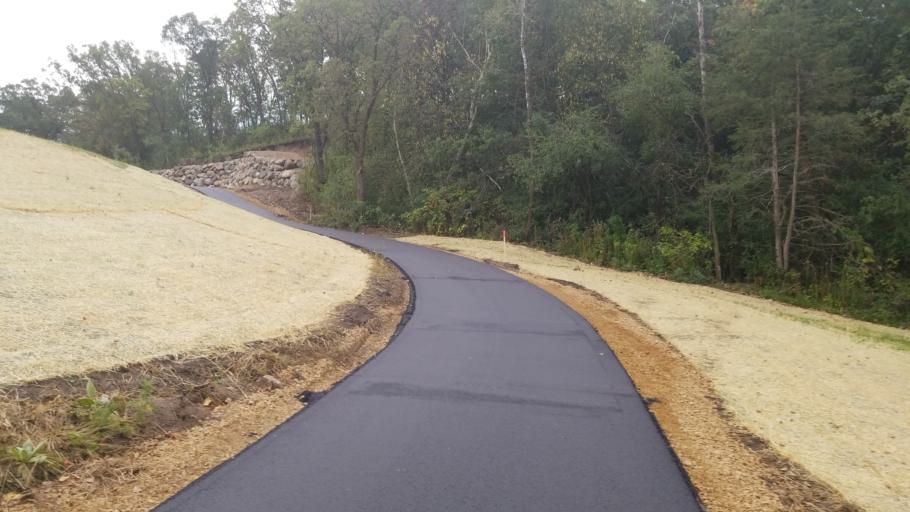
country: US
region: Wisconsin
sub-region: Saint Croix County
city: Hudson
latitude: 44.9707
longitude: -92.7305
